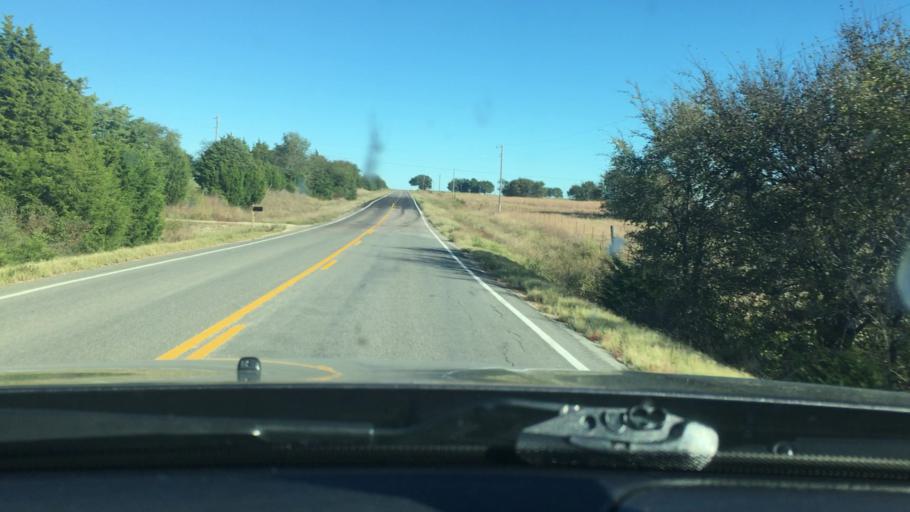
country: US
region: Oklahoma
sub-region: Johnston County
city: Tishomingo
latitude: 34.1527
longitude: -96.7059
